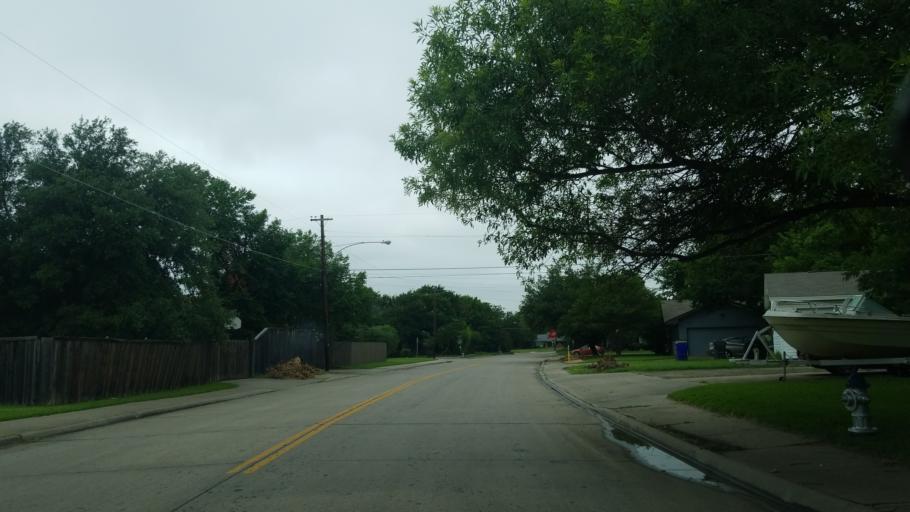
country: US
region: Texas
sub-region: Dallas County
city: Farmers Branch
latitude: 32.9012
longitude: -96.8629
